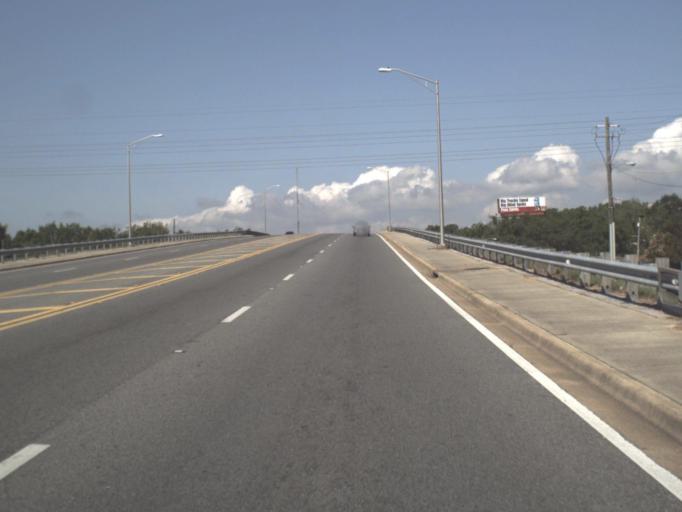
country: US
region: Florida
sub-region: Escambia County
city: Goulding
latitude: 30.4462
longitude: -87.2223
